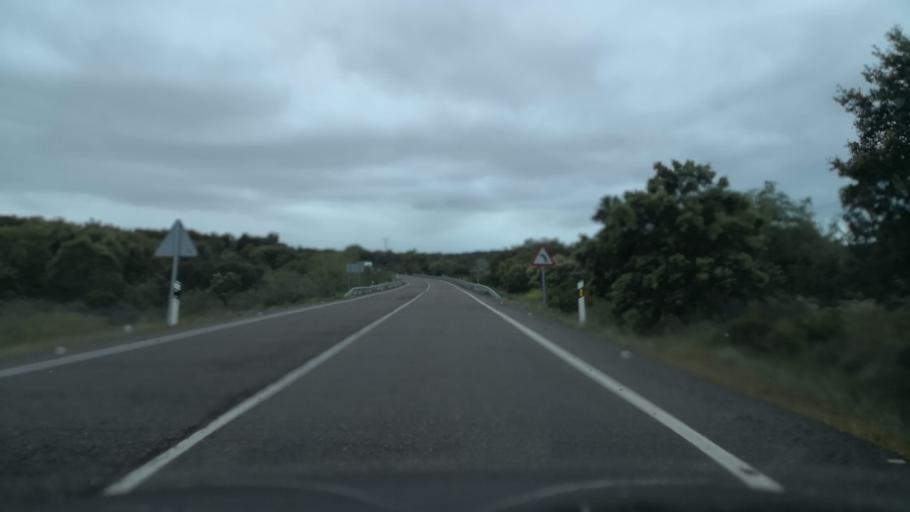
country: ES
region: Extremadura
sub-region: Provincia de Badajoz
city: La Roca de la Sierra
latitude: 39.1371
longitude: -6.6586
